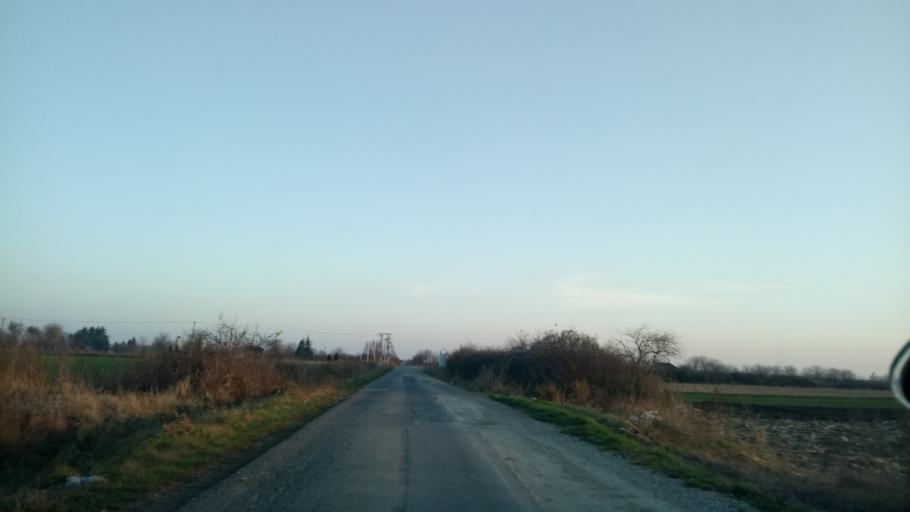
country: RS
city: Surduk
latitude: 45.1009
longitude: 20.2887
